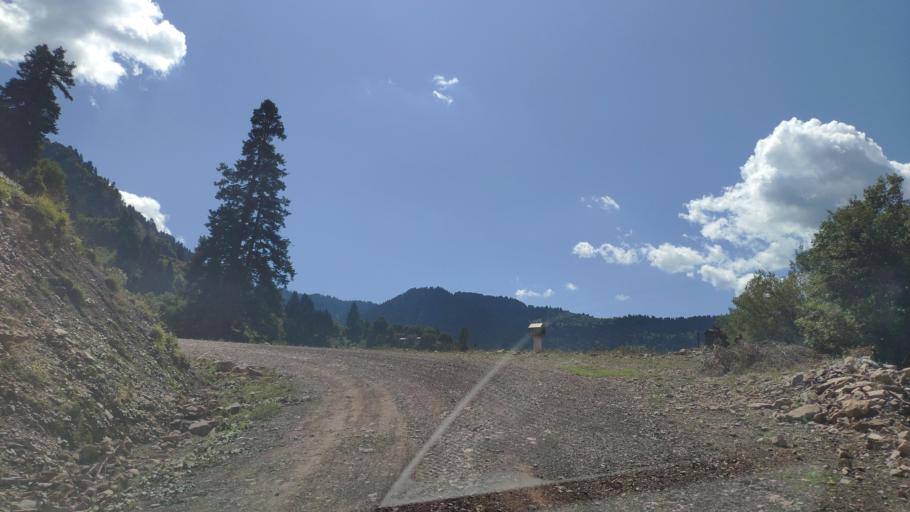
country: GR
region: Central Greece
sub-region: Nomos Evrytanias
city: Kerasochori
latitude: 39.1403
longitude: 21.6588
